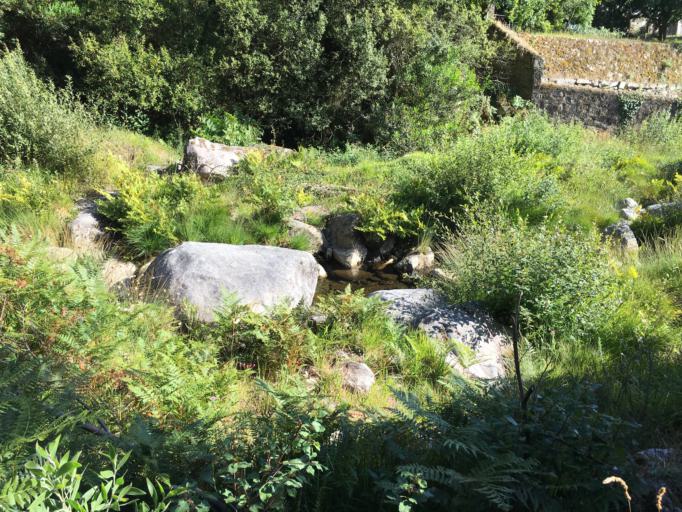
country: PT
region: Viana do Castelo
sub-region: Viana do Castelo
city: Areosa
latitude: 41.7228
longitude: -8.8483
